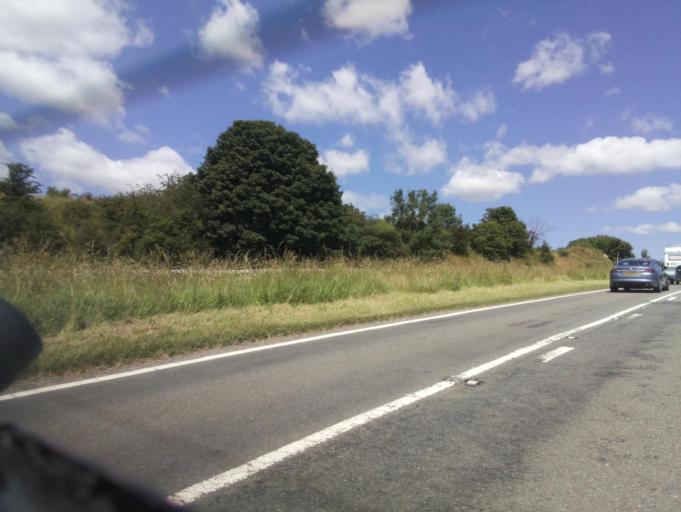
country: GB
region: England
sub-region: Derbyshire
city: Ashbourne
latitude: 53.1033
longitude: -1.7684
